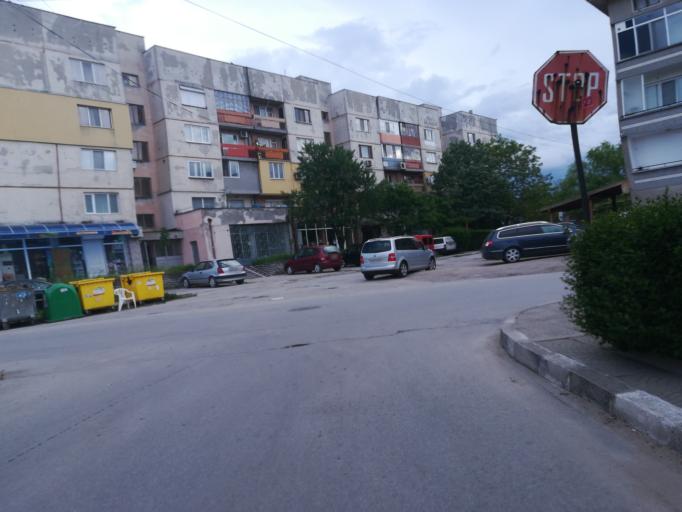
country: BG
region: Stara Zagora
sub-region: Obshtina Chirpan
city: Chirpan
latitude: 42.0979
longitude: 25.2287
